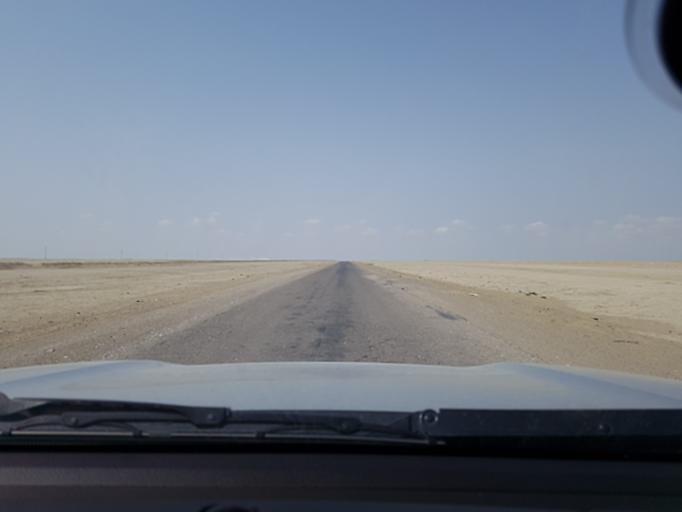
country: TM
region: Balkan
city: Gumdag
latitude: 38.6844
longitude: 54.4194
